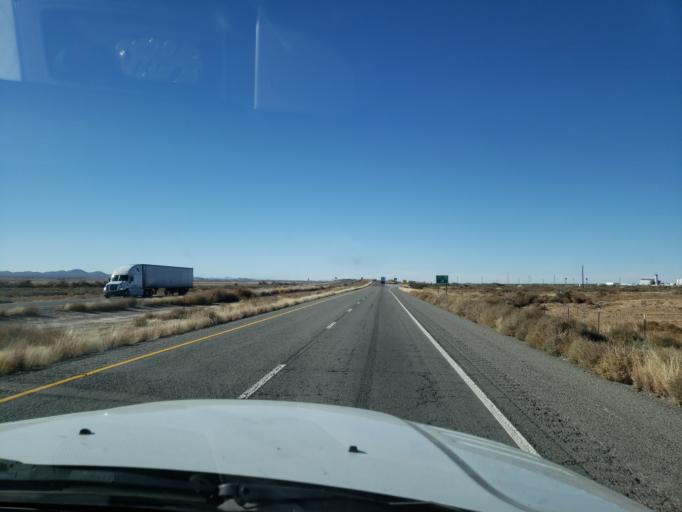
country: US
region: New Mexico
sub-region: Hidalgo County
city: Lordsburg
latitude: 32.3093
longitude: -108.6020
